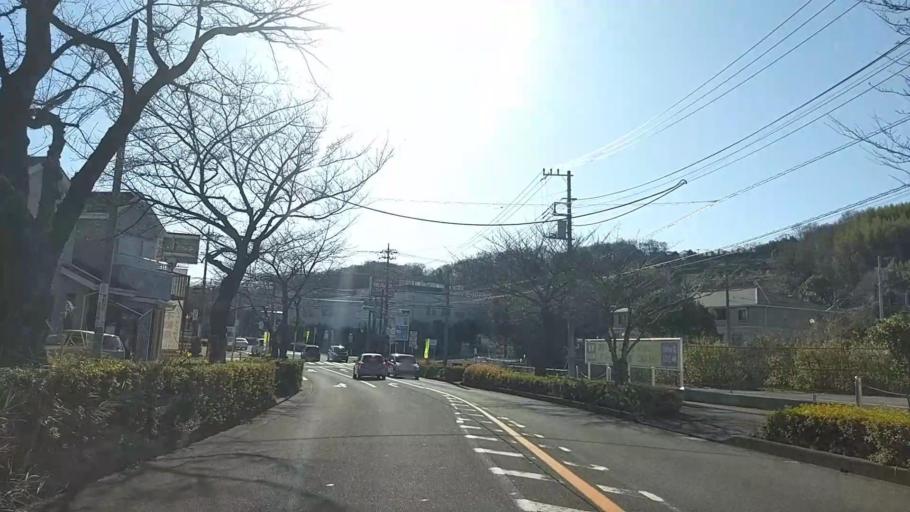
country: JP
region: Kanagawa
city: Hadano
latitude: 35.3666
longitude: 139.2107
